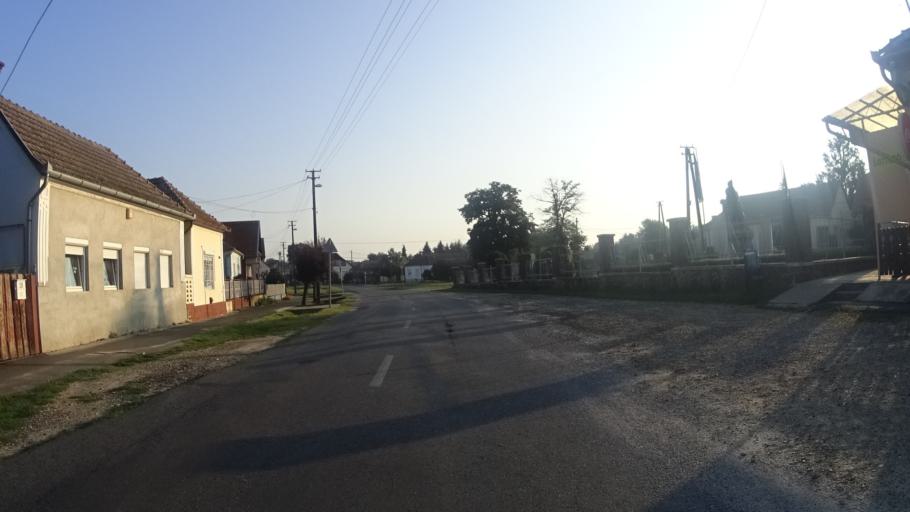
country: HU
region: Zala
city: Zalakomar
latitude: 46.5479
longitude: 17.1745
